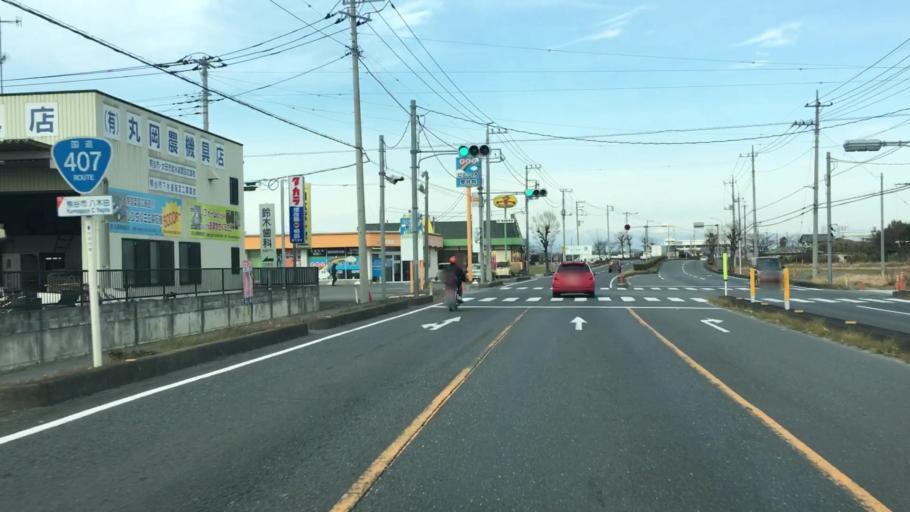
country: JP
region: Saitama
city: Menuma
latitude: 36.2179
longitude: 139.3682
